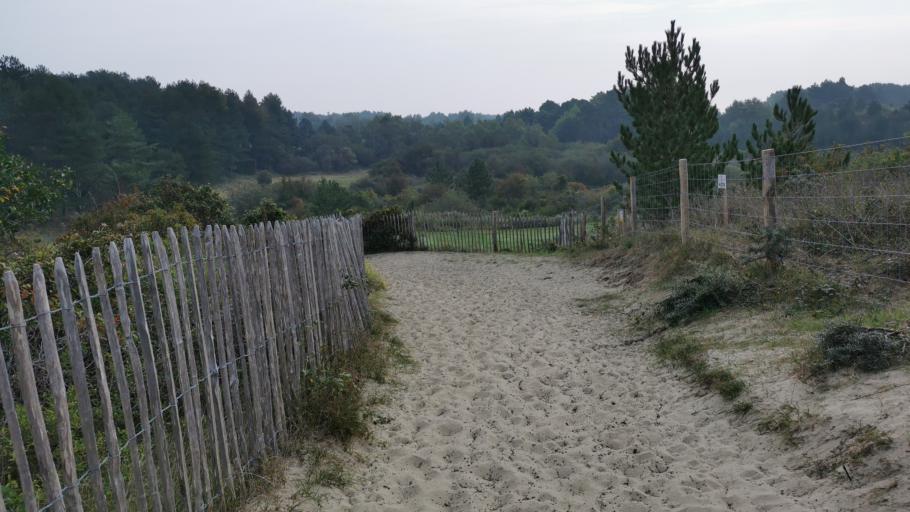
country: FR
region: Picardie
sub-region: Departement de la Somme
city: Fort-Mahon-Plage
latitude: 50.3308
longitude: 1.5584
